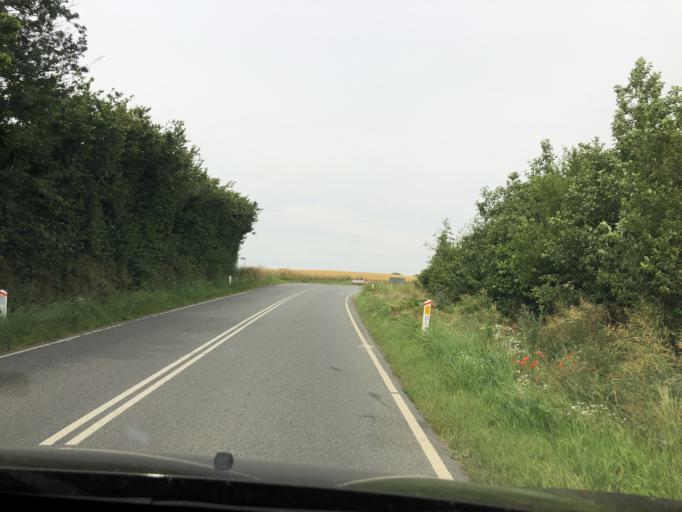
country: DK
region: South Denmark
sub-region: Assens Kommune
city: Glamsbjerg
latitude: 55.3052
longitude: 10.0525
